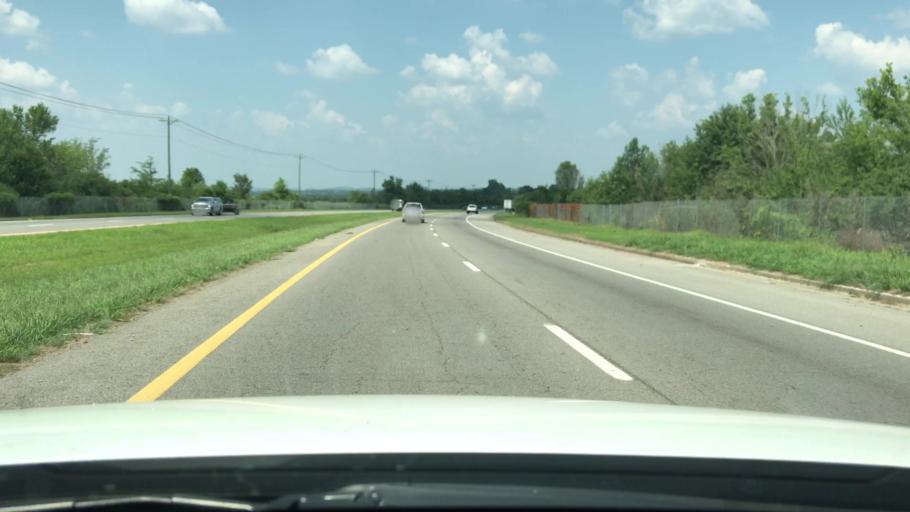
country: US
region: Tennessee
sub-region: Sumner County
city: Gallatin
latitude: 36.3631
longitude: -86.4492
